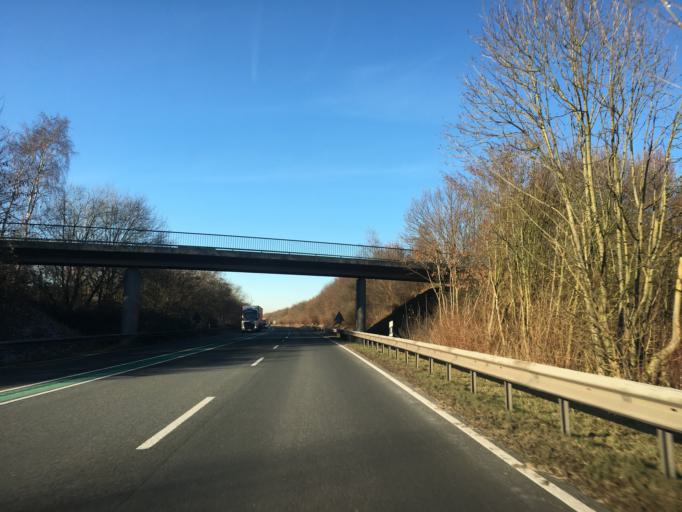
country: DE
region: North Rhine-Westphalia
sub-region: Regierungsbezirk Munster
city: Laer
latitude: 52.0983
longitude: 7.4031
